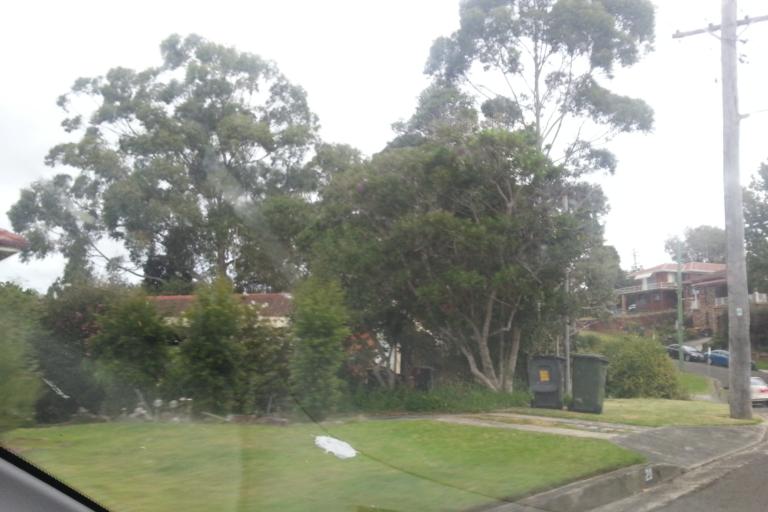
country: AU
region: New South Wales
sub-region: Wollongong
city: Keiraville
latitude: -34.4101
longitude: 150.8686
